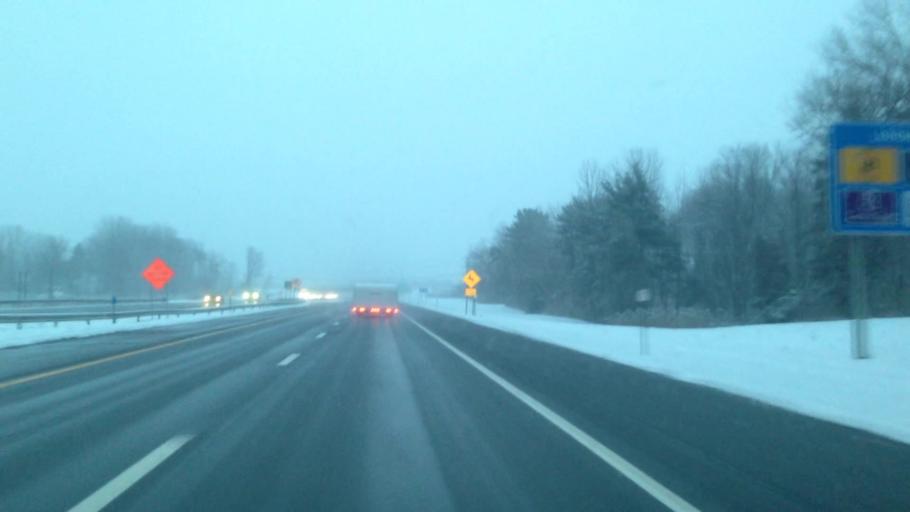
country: US
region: New York
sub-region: Oneida County
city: Sherrill
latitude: 43.1248
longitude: -75.5962
